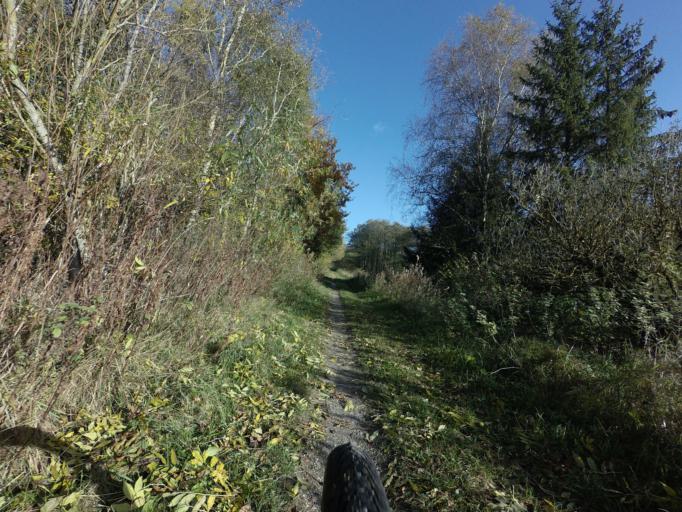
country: DK
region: Central Jutland
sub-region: Syddjurs Kommune
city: Ryomgard
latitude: 56.4173
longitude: 10.5695
